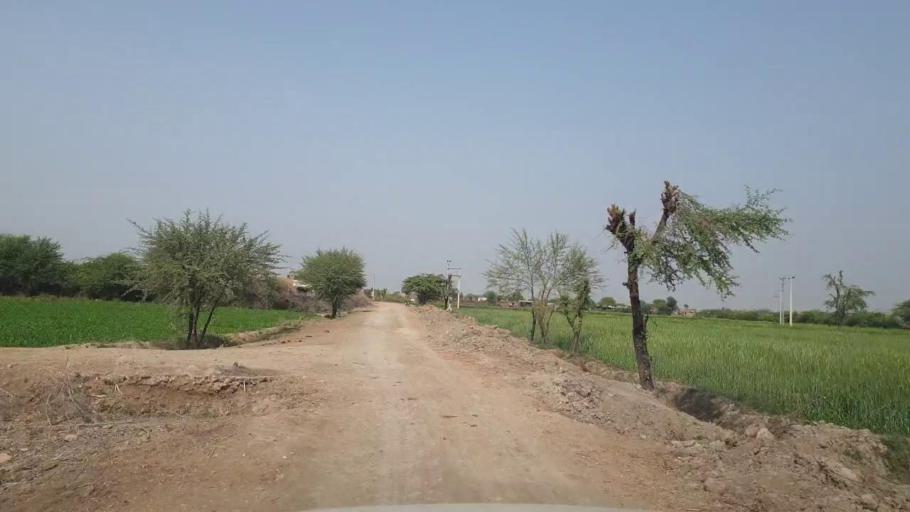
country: PK
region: Sindh
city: Dhoro Naro
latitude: 25.4792
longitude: 69.6366
